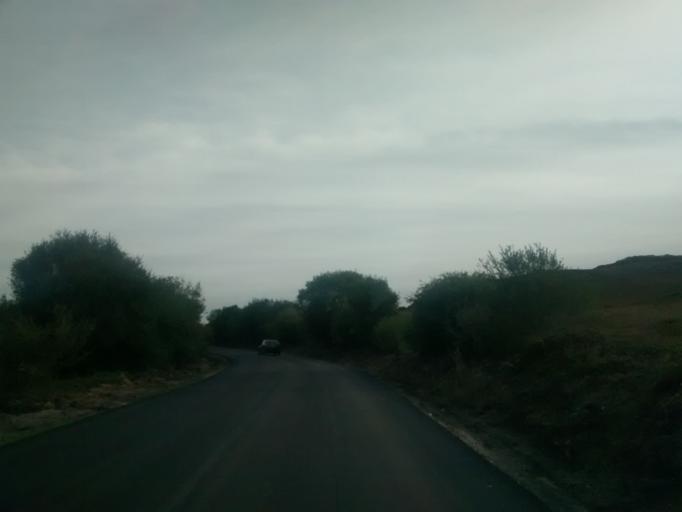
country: ES
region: Castille and Leon
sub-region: Provincia de Burgos
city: Arija
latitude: 42.9890
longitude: -3.9430
